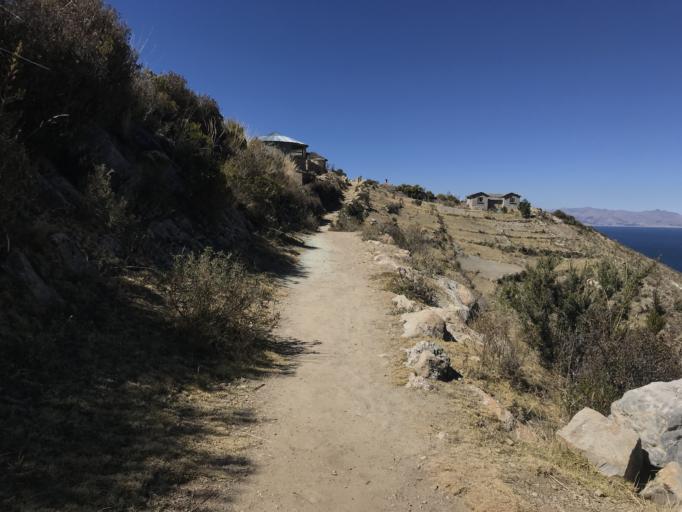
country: BO
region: La Paz
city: Yumani
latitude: -16.0319
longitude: -69.1563
